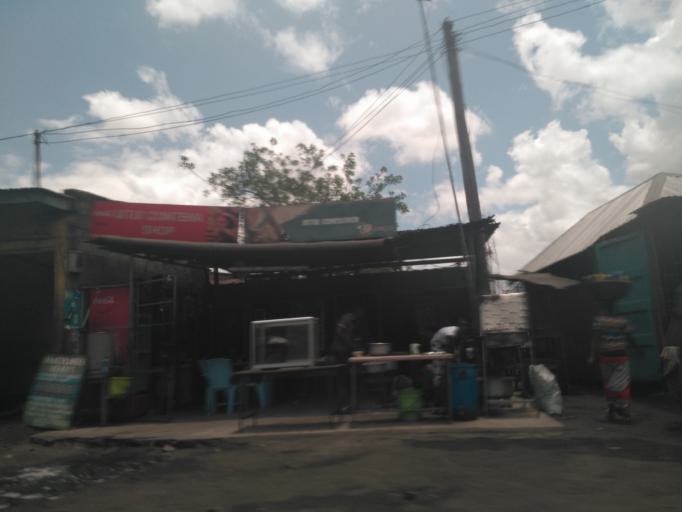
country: TZ
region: Dar es Salaam
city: Dar es Salaam
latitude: -6.8643
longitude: 39.2651
